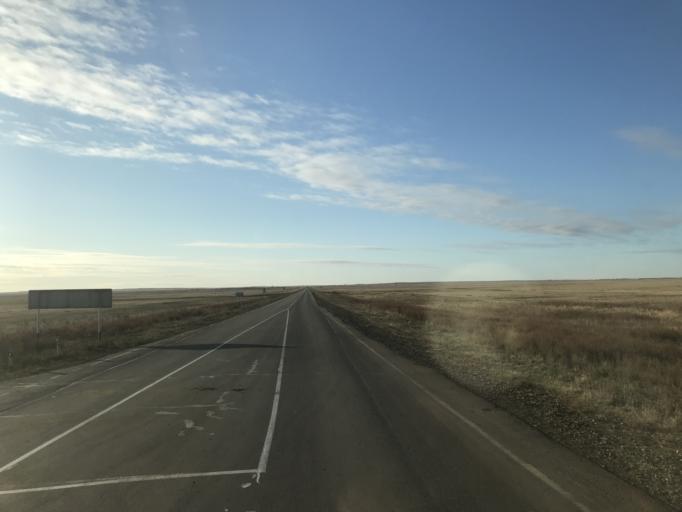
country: KZ
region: Qostanay
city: Ordzhonikidze
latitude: 52.0905
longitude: 61.9881
